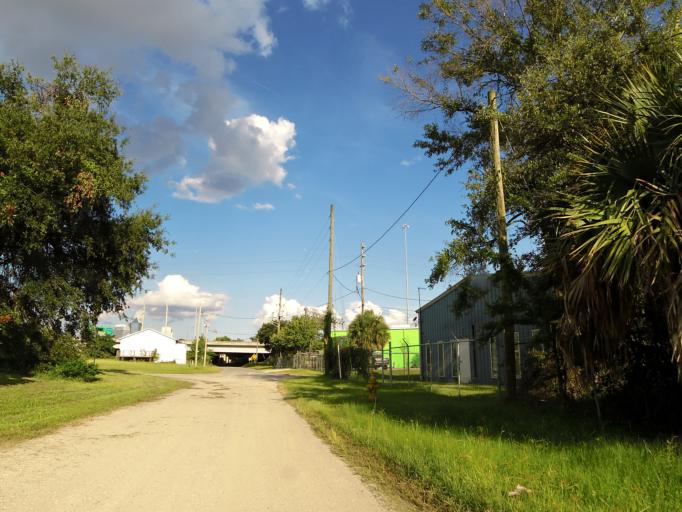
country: US
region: Florida
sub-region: Duval County
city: Jacksonville
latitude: 30.3282
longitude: -81.6801
